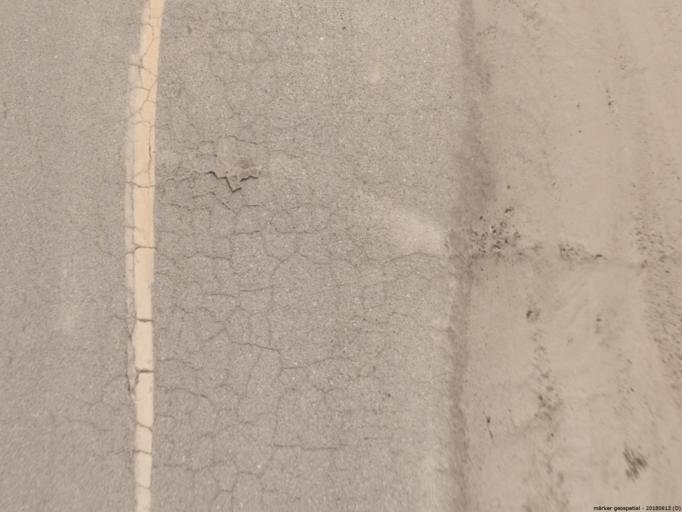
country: US
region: California
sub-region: Madera County
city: Chowchilla
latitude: 37.0761
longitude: -120.3409
